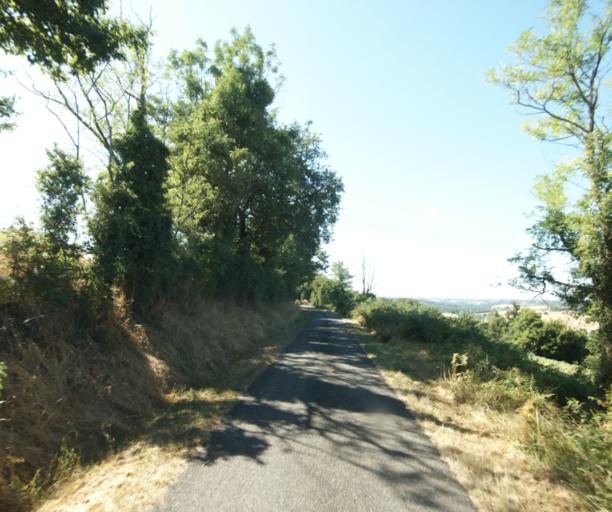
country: FR
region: Midi-Pyrenees
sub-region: Departement de la Haute-Garonne
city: Saint-Felix-Lauragais
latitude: 43.5226
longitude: 1.9088
